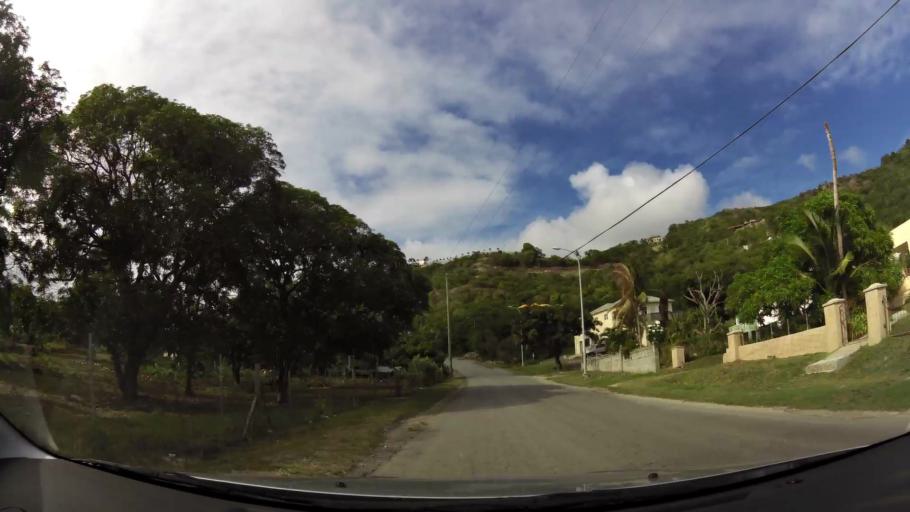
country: AG
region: Saint Paul
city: Falmouth
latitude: 17.0269
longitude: -61.7812
